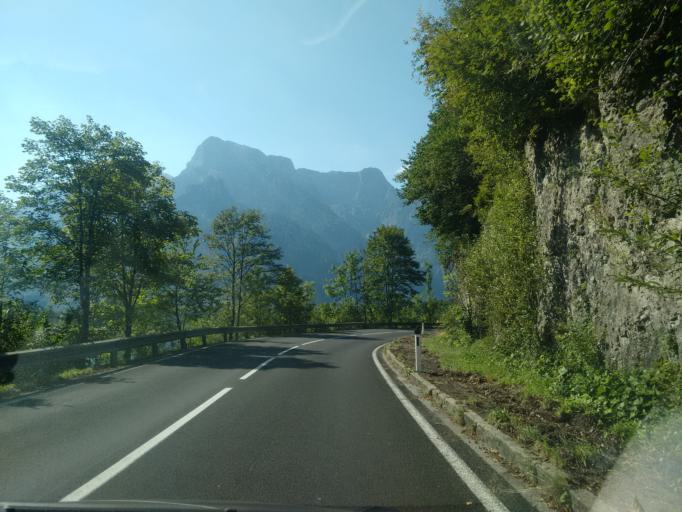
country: AT
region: Upper Austria
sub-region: Politischer Bezirk Gmunden
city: Gruenau im Almtal
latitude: 47.7491
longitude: 13.9529
